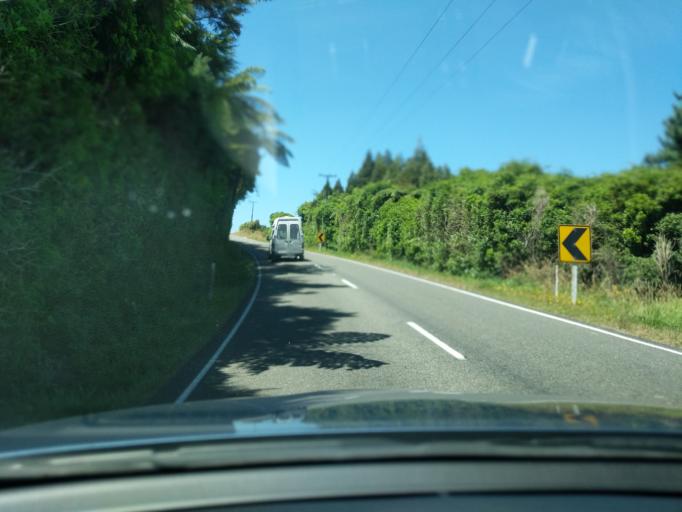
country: NZ
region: Tasman
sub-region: Tasman District
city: Takaka
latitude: -40.6940
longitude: 172.6394
